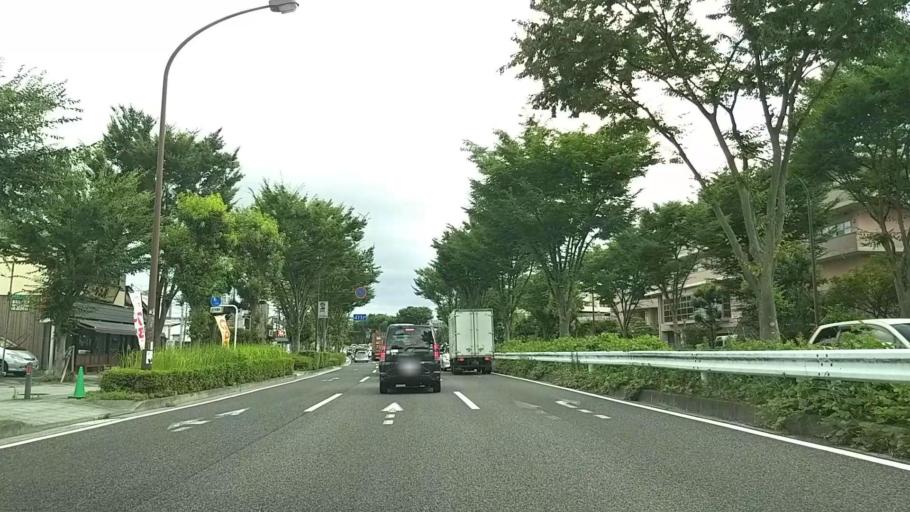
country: JP
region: Kanagawa
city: Yokohama
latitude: 35.4115
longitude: 139.5607
